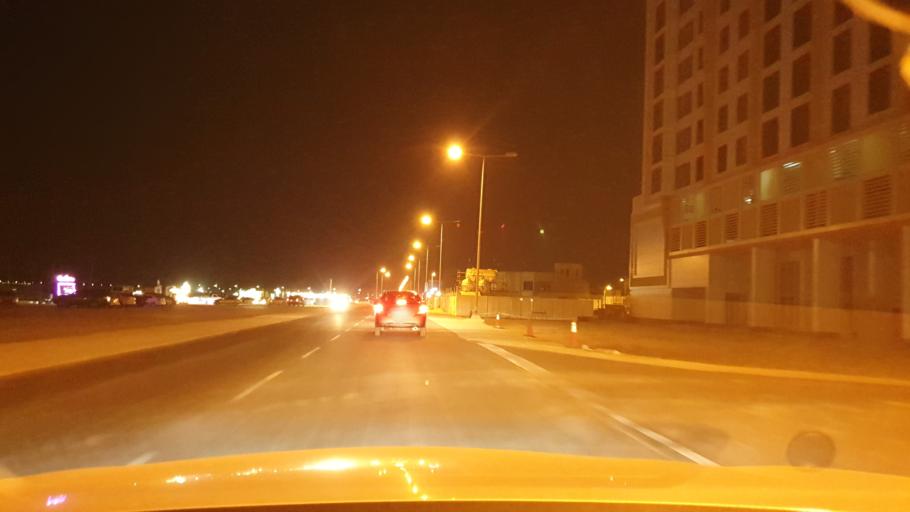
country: BH
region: Muharraq
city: Al Muharraq
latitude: 26.2645
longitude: 50.5945
